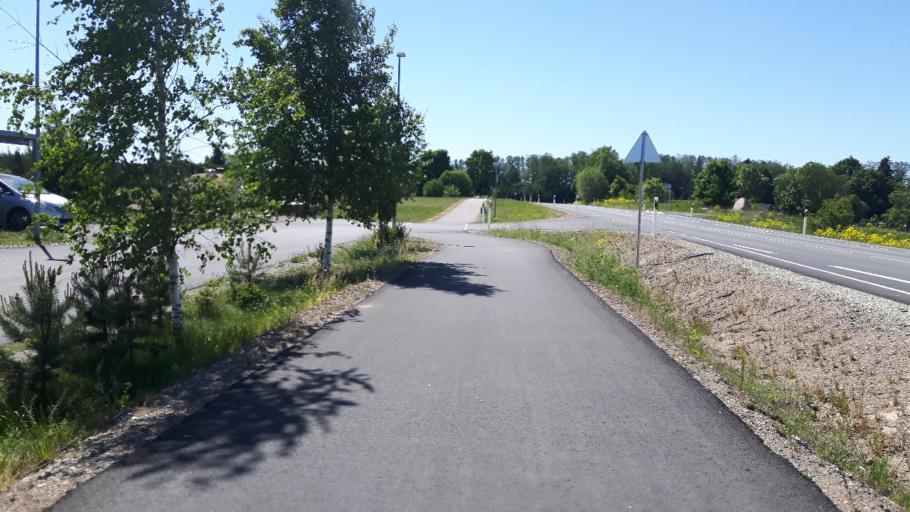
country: EE
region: Harju
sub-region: Kuusalu vald
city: Kuusalu
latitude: 59.4567
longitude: 25.4476
